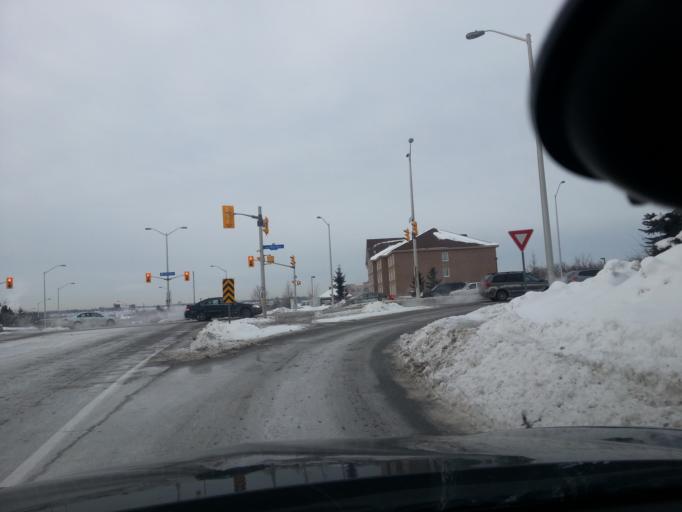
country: CA
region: Ontario
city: Bells Corners
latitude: 45.3025
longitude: -75.9072
